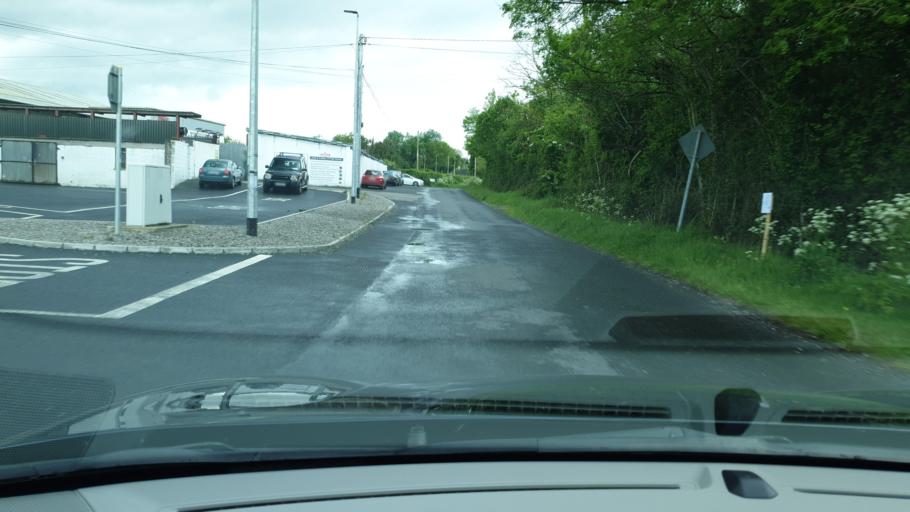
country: IE
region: Leinster
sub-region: Laois
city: Portlaoise
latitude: 53.0338
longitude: -7.3287
